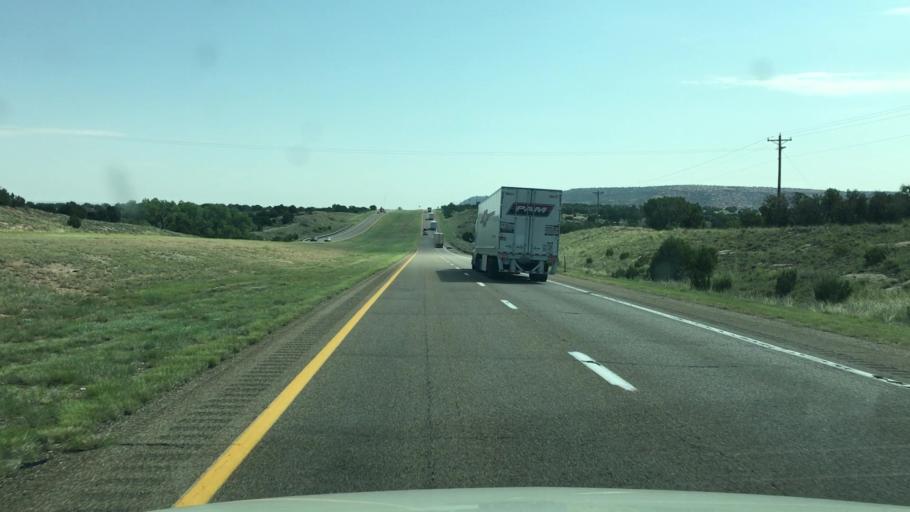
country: US
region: New Mexico
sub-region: Guadalupe County
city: Santa Rosa
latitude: 35.0180
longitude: -104.4391
